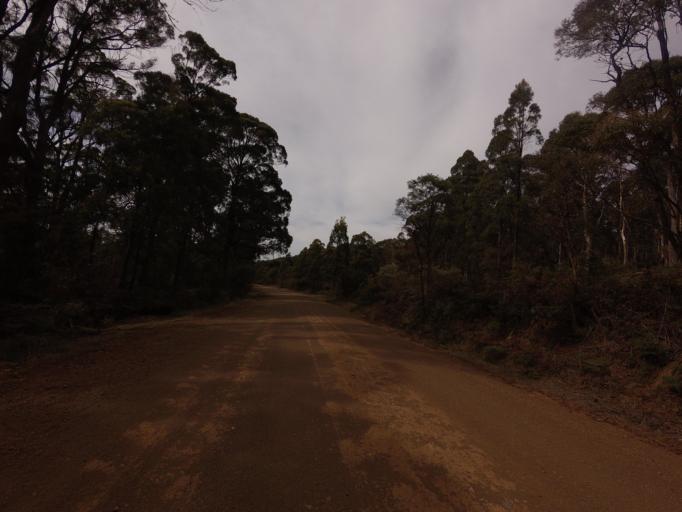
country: AU
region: Tasmania
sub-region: Sorell
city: Sorell
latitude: -42.4898
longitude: 147.6210
